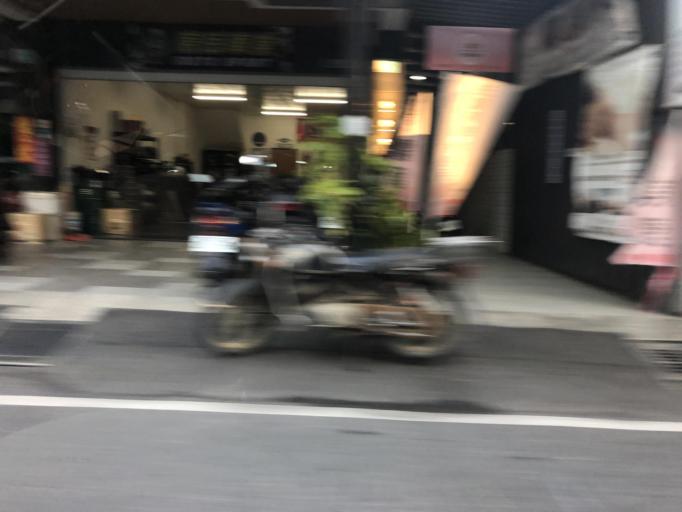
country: TW
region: Taiwan
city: Xinying
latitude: 23.1808
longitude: 120.2516
